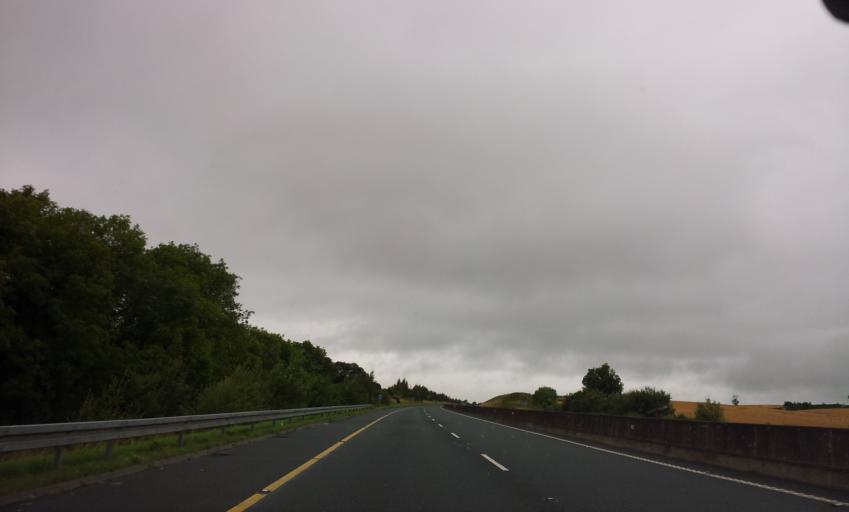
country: IE
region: Munster
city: Cahir
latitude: 52.4253
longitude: -7.9150
